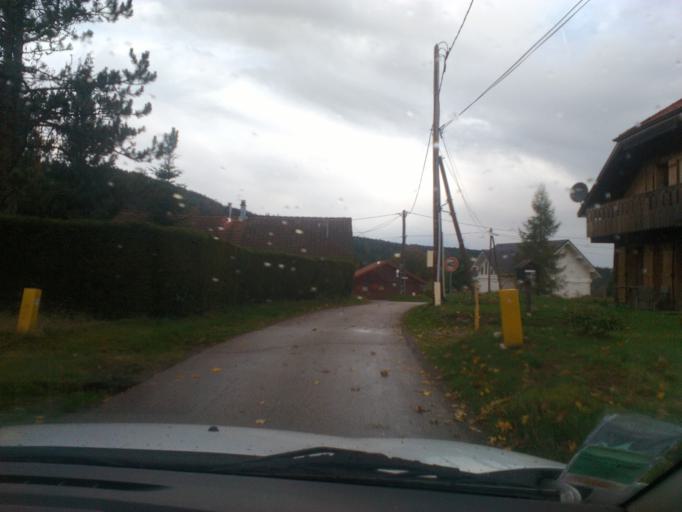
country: FR
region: Lorraine
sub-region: Departement des Vosges
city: Xonrupt-Longemer
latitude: 48.1239
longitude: 6.9102
